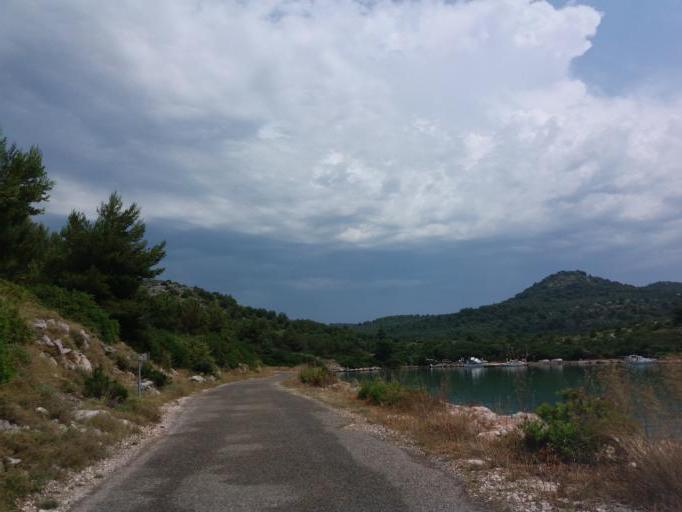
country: HR
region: Zadarska
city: Sali
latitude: 43.9248
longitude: 15.1337
